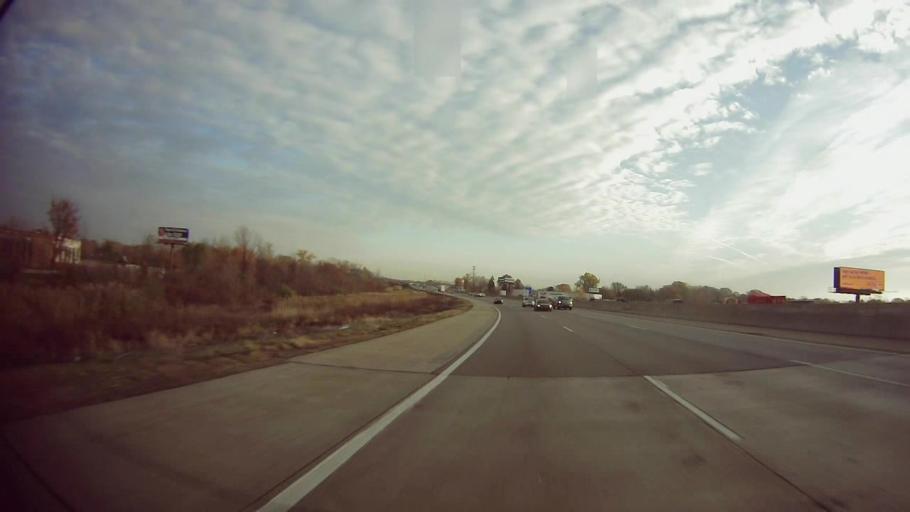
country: US
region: Michigan
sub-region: Macomb County
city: Saint Clair Shores
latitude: 42.5412
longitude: -82.8848
